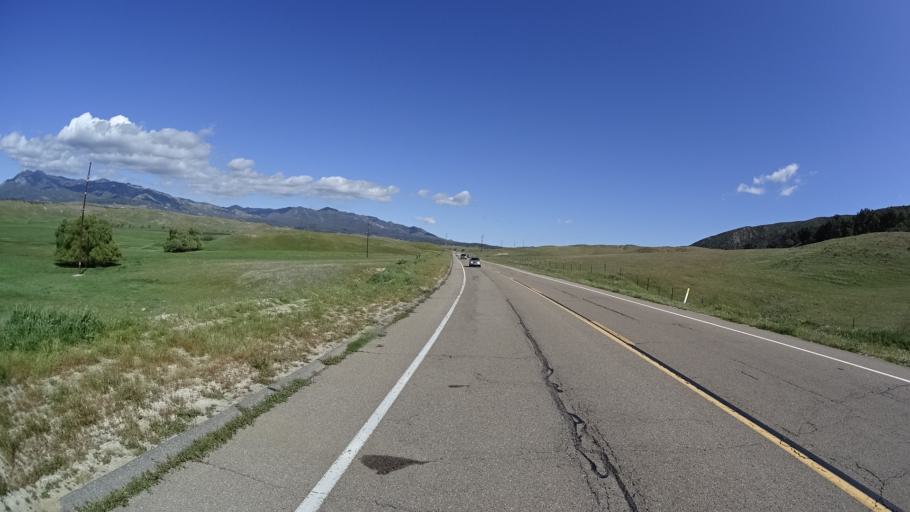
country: US
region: California
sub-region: San Diego County
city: Julian
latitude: 33.2326
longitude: -116.6426
